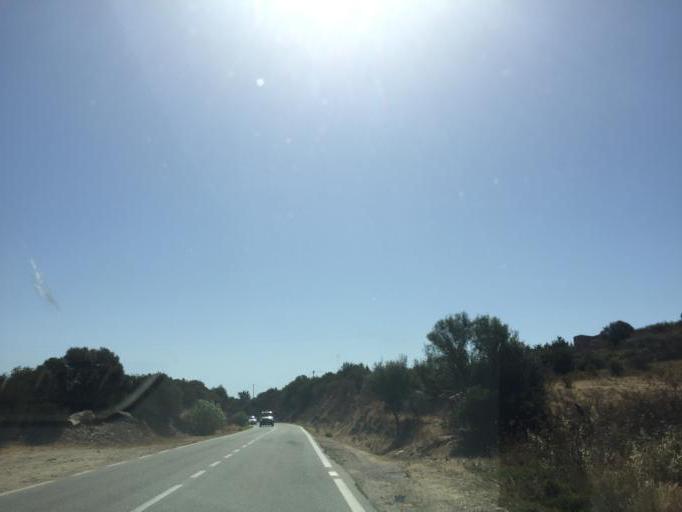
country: IT
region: Sardinia
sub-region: Provincia di Olbia-Tempio
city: San Teodoro
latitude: 40.7609
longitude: 9.6566
